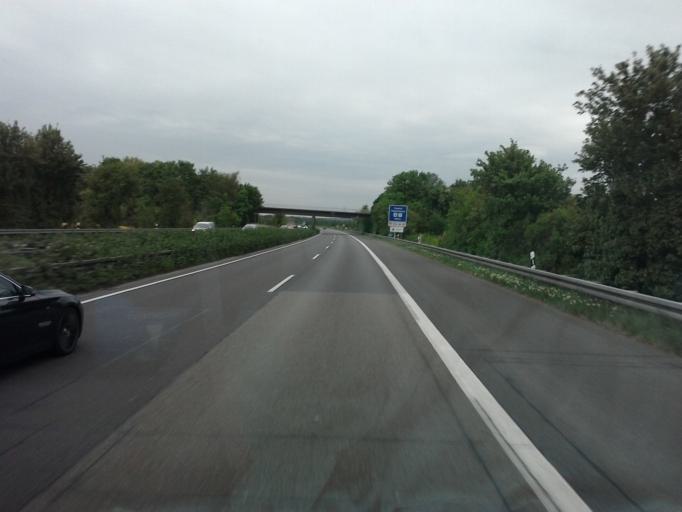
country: DE
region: North Rhine-Westphalia
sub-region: Regierungsbezirk Koln
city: Rheinbach
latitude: 50.6548
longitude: 6.9271
